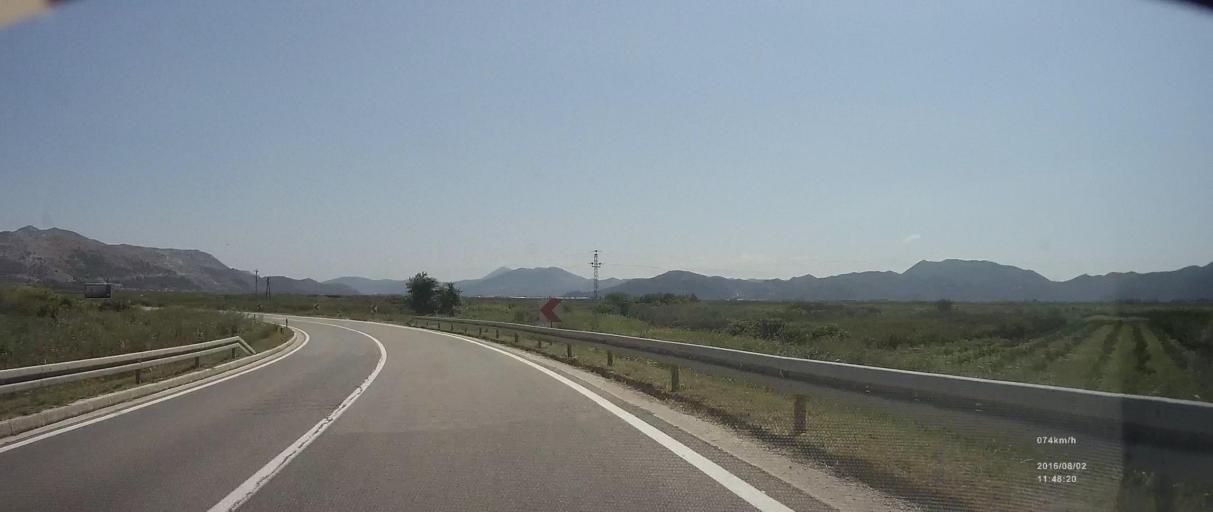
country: HR
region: Dubrovacko-Neretvanska
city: Komin
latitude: 43.0347
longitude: 17.4879
